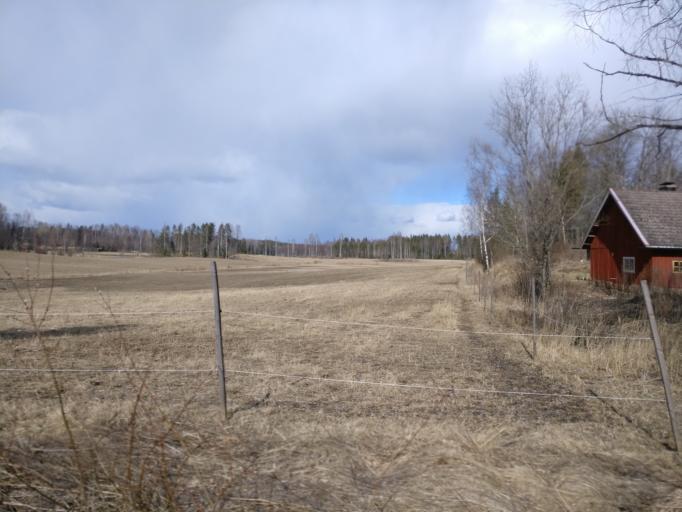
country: FI
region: Varsinais-Suomi
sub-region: Salo
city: Suomusjaervi
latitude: 60.3174
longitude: 23.7090
